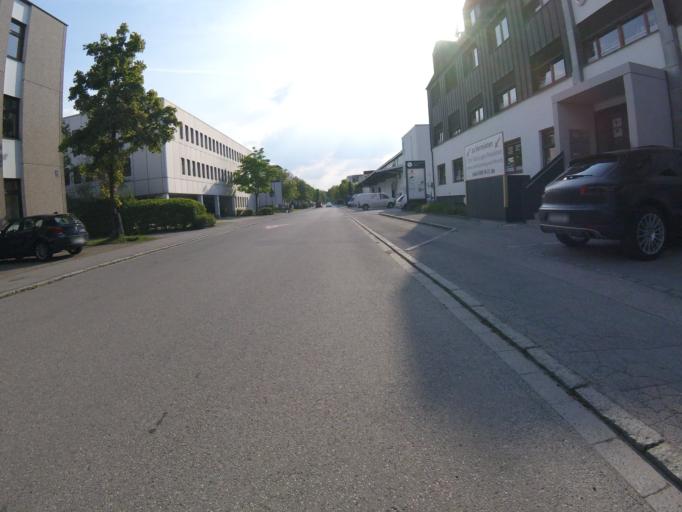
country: DE
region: Bavaria
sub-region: Upper Bavaria
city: Ottobrunn
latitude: 48.0546
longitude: 11.6772
